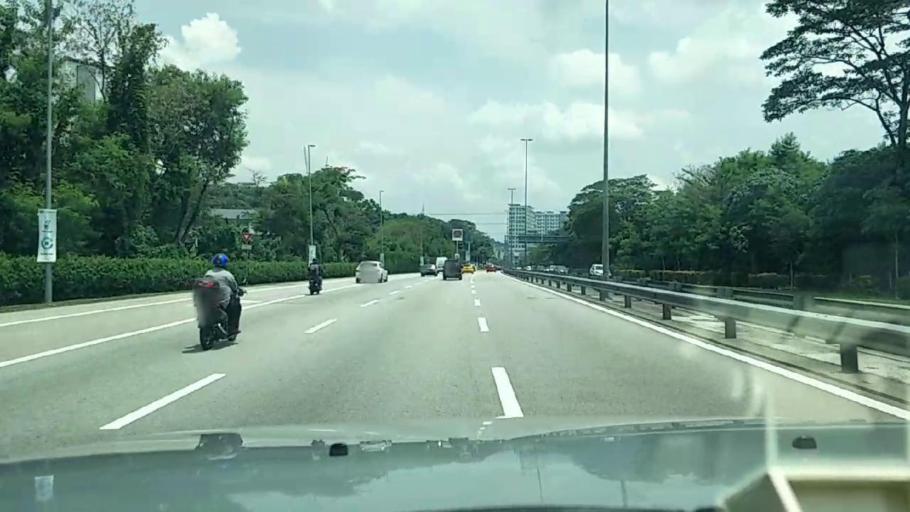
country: MY
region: Kuala Lumpur
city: Kuala Lumpur
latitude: 3.0940
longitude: 101.6844
